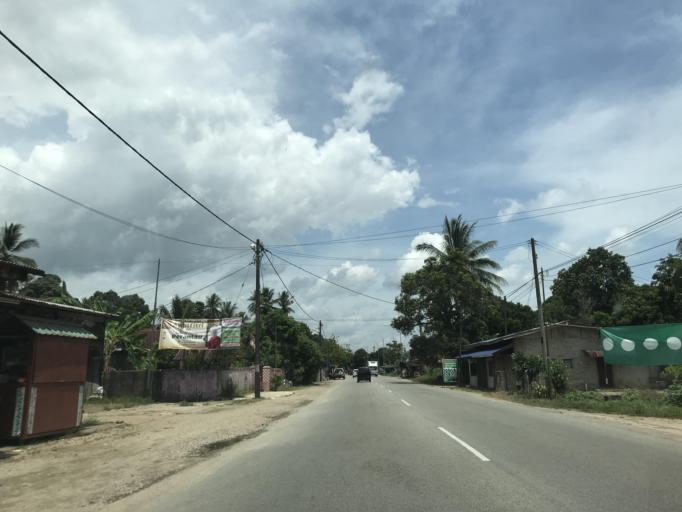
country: MY
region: Kelantan
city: Pasir Mas
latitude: 6.0533
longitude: 102.1905
